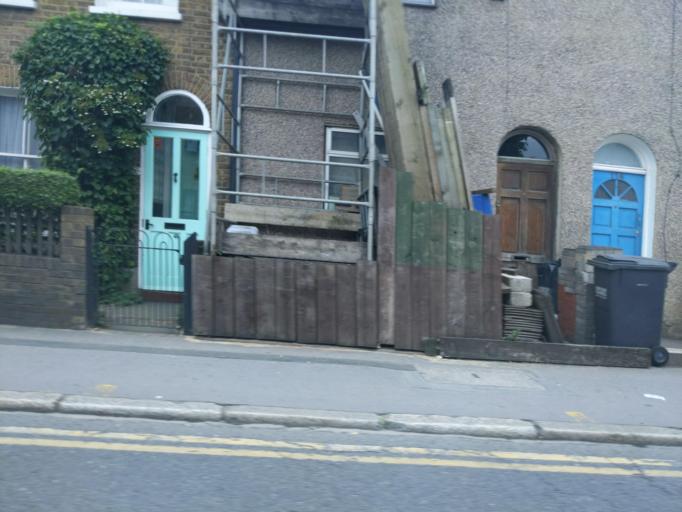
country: GB
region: England
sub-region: Greater London
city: South Croydon
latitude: 51.3658
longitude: -0.1002
